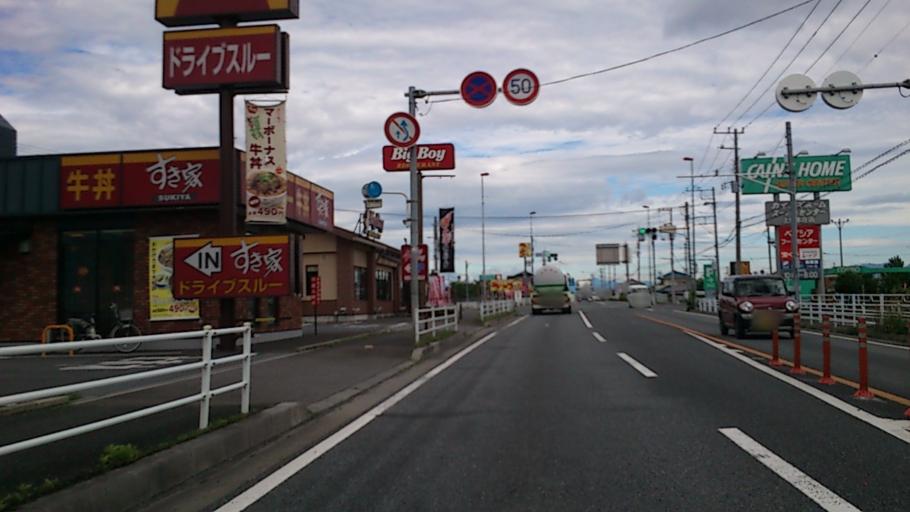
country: JP
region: Saitama
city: Honjo
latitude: 36.2564
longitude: 139.1575
